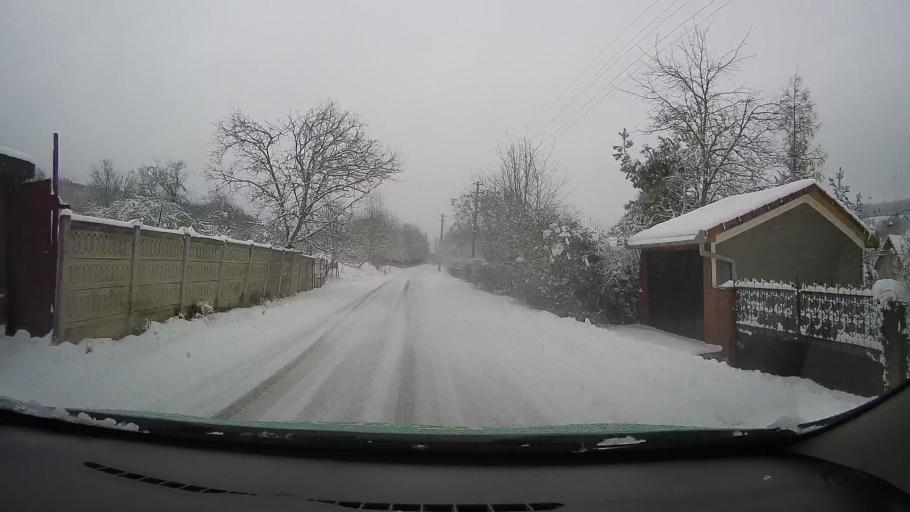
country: RO
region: Hunedoara
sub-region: Comuna Carjiti
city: Carjiti
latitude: 45.8272
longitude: 22.8500
